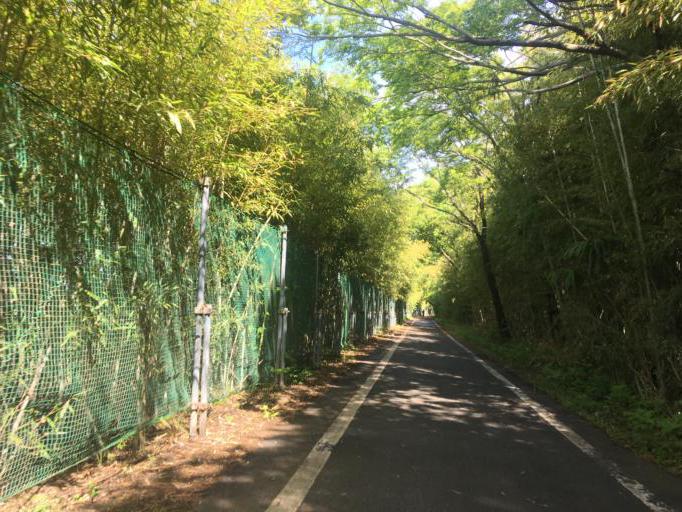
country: JP
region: Saitama
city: Shiki
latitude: 35.8631
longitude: 139.5855
